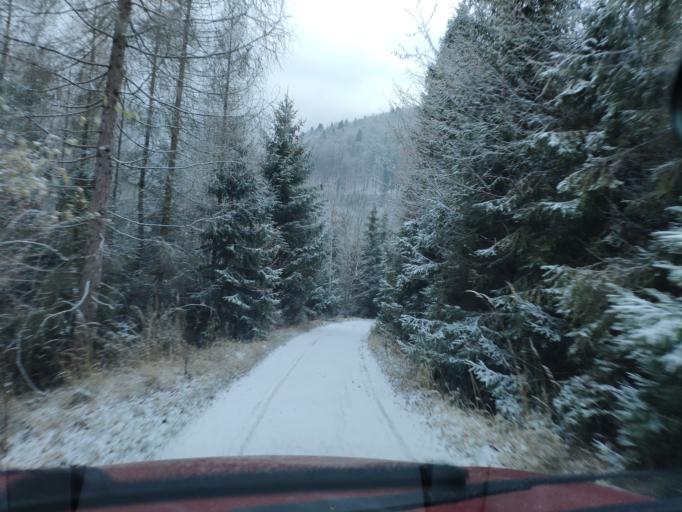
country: SK
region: Kosicky
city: Spisska Nova Ves
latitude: 48.8117
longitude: 20.5162
